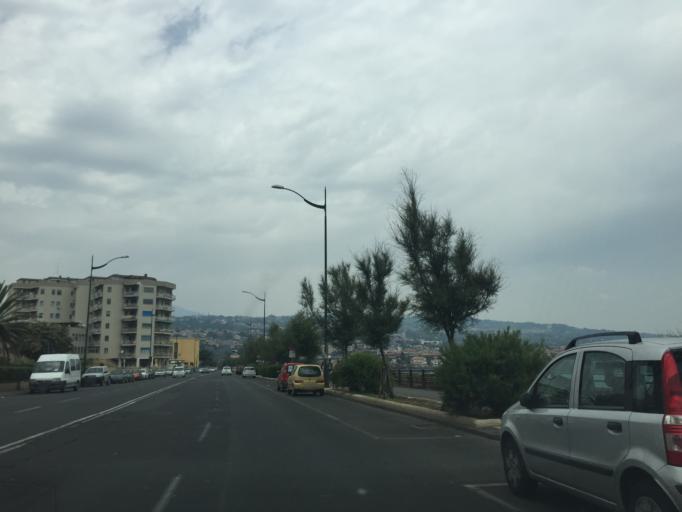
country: IT
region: Sicily
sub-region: Catania
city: Cerza
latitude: 37.5251
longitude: 15.1165
